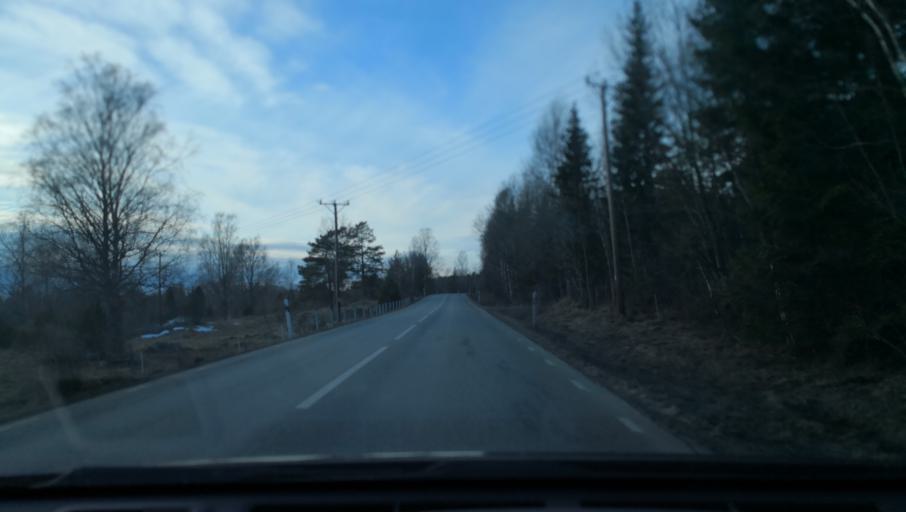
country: SE
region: Uppsala
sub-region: Osthammars Kommun
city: Gimo
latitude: 60.3370
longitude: 18.2207
